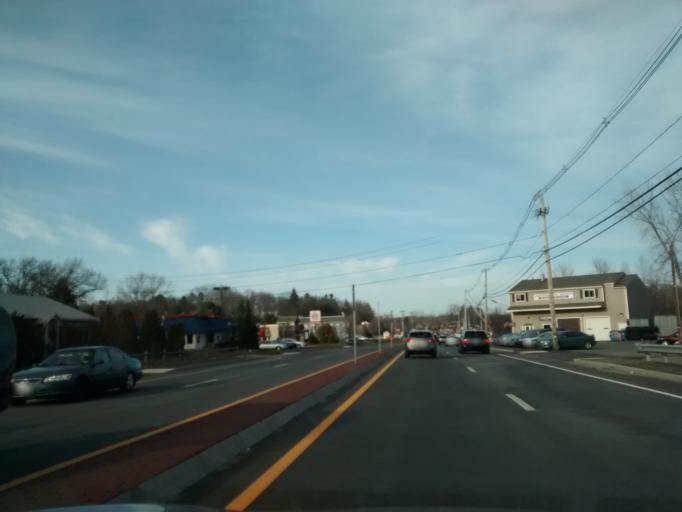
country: US
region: Massachusetts
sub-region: Worcester County
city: Auburn
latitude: 42.1776
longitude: -71.8725
